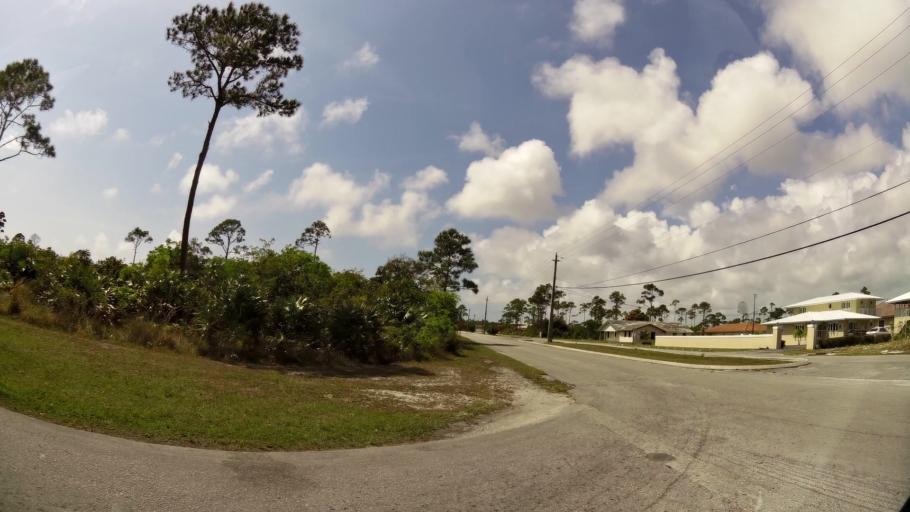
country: BS
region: Freeport
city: Freeport
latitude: 26.5065
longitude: -78.7222
